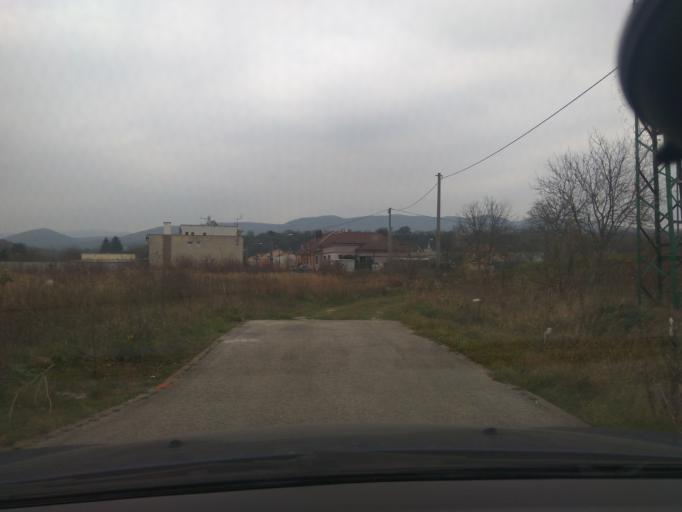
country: SK
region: Trnavsky
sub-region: Okres Trnava
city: Piestany
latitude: 48.6078
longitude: 17.8620
